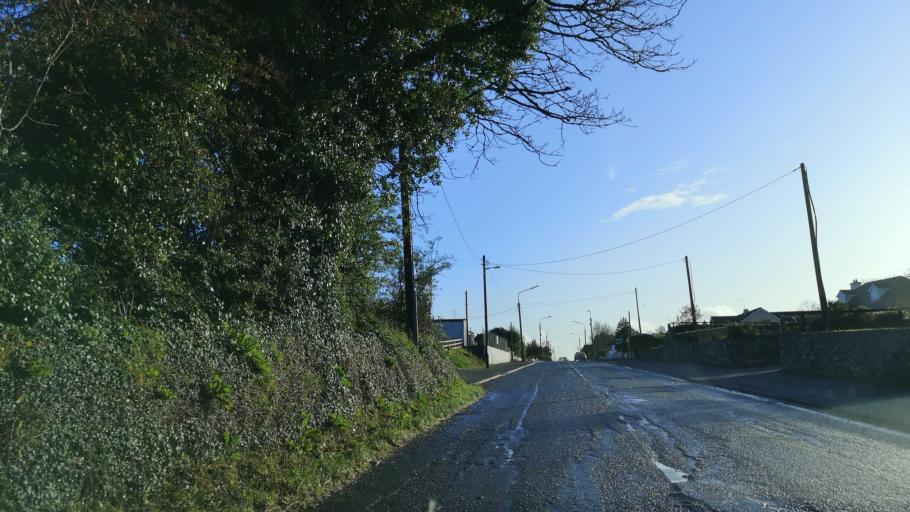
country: IE
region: Connaught
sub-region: Roscommon
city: Castlerea
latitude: 53.7769
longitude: -8.4892
